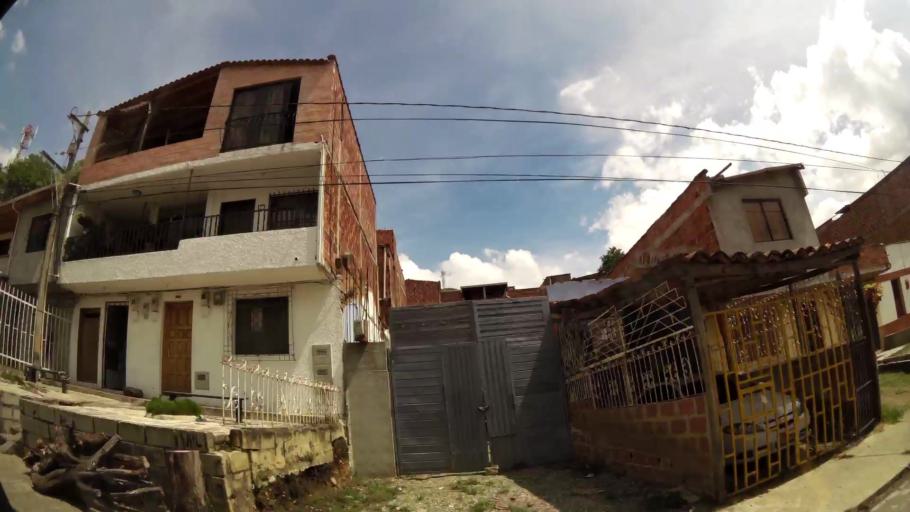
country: CO
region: Antioquia
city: Bello
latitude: 6.3443
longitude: -75.5514
